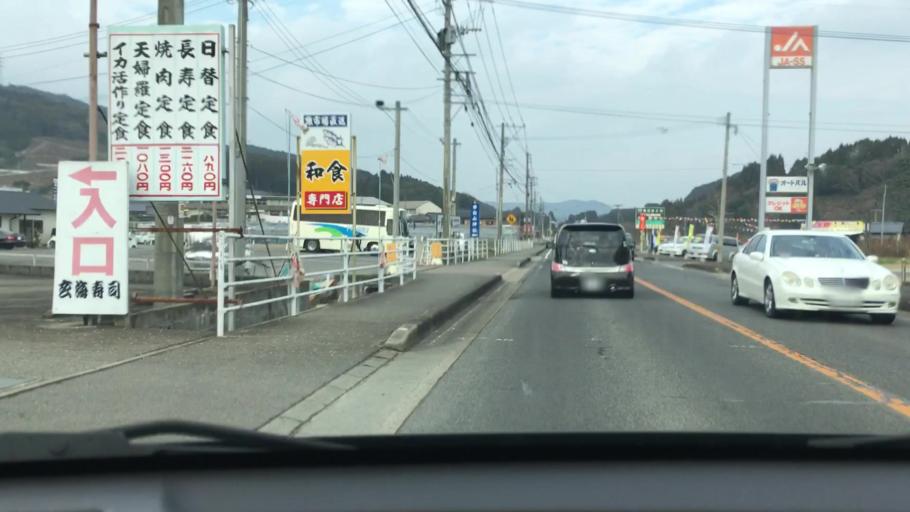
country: JP
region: Saga Prefecture
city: Imaricho-ko
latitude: 33.3149
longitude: 129.9287
